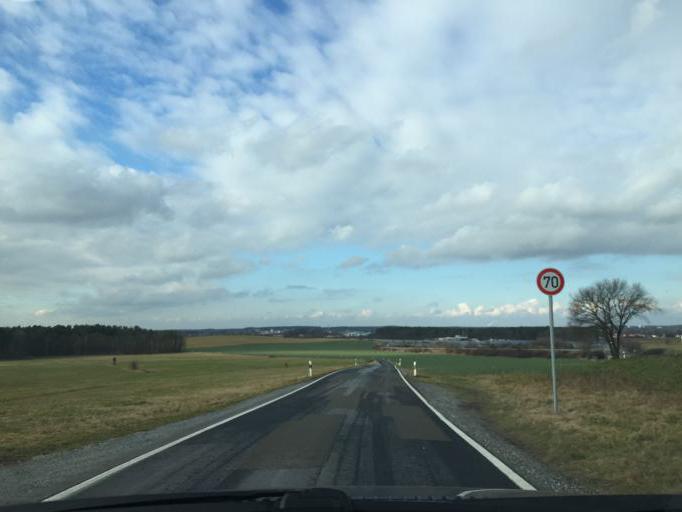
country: DE
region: Saxony
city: Ottendorf-Okrilla
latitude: 51.1676
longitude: 13.8620
